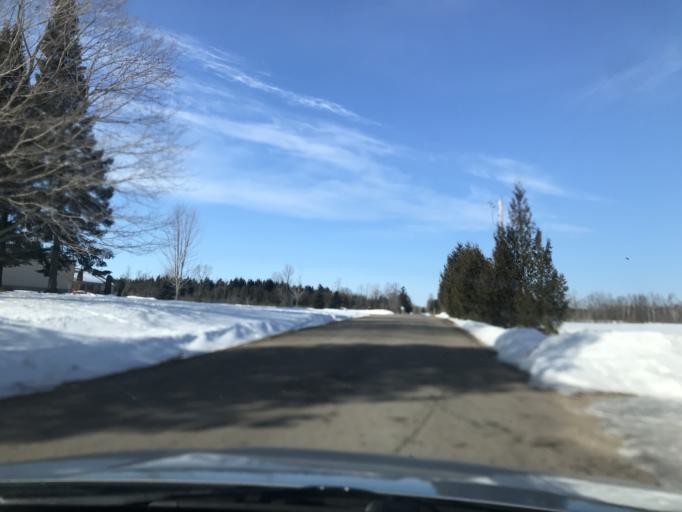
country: US
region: Wisconsin
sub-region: Oconto County
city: Oconto Falls
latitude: 44.9232
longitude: -88.1674
